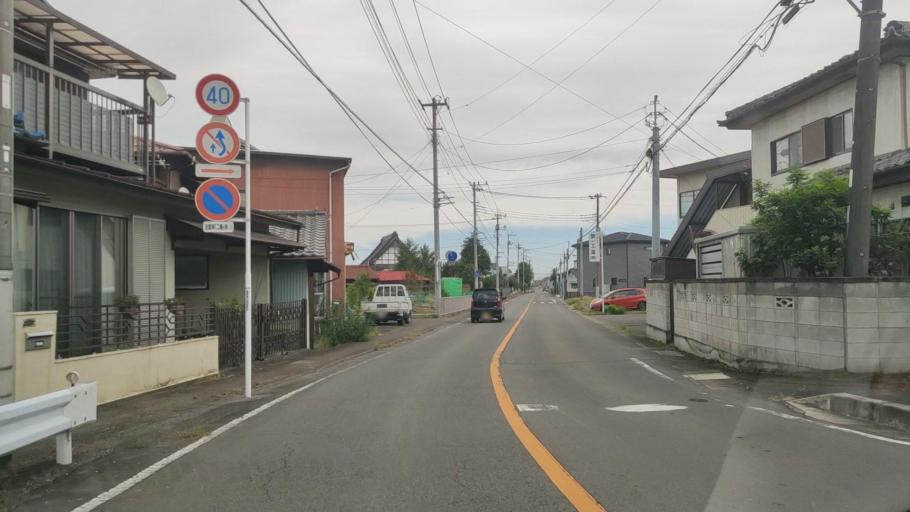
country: JP
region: Gunma
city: Takasaki
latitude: 36.3628
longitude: 138.9781
